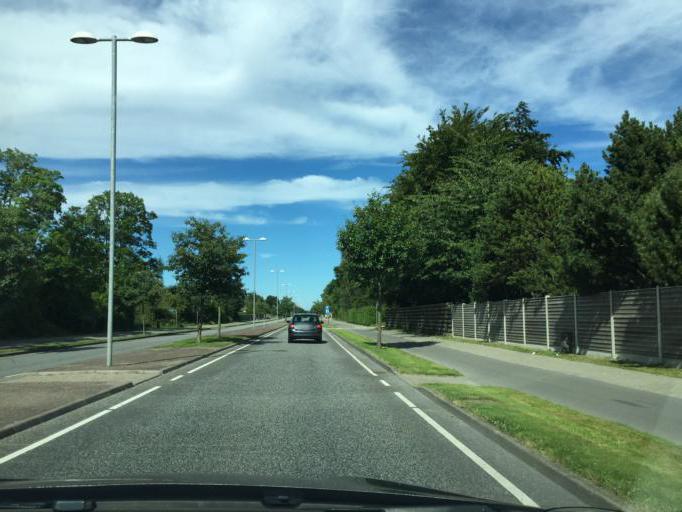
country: DK
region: Zealand
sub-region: Solrod Kommune
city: Solrod Strand
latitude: 55.5160
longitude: 12.2073
